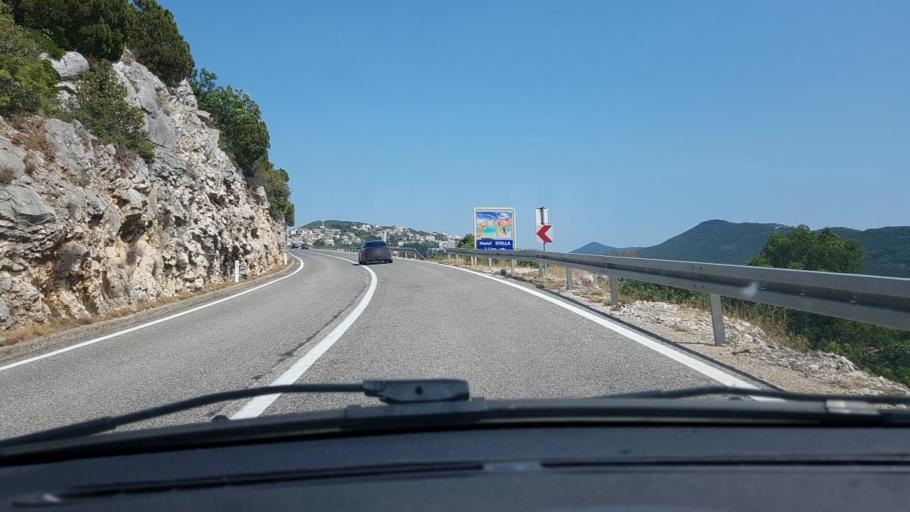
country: BA
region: Federation of Bosnia and Herzegovina
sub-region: Hercegovacko-Bosanski Kanton
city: Neum
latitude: 42.9302
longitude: 17.6013
